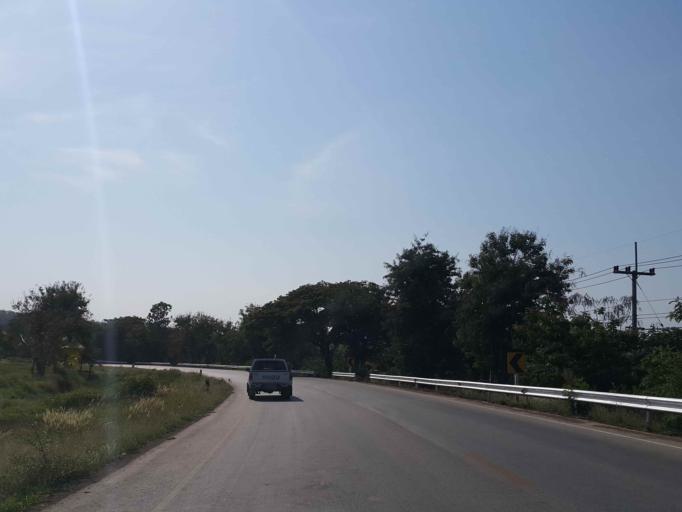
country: TH
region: Sukhothai
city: Thung Saliam
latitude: 17.3436
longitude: 99.5987
